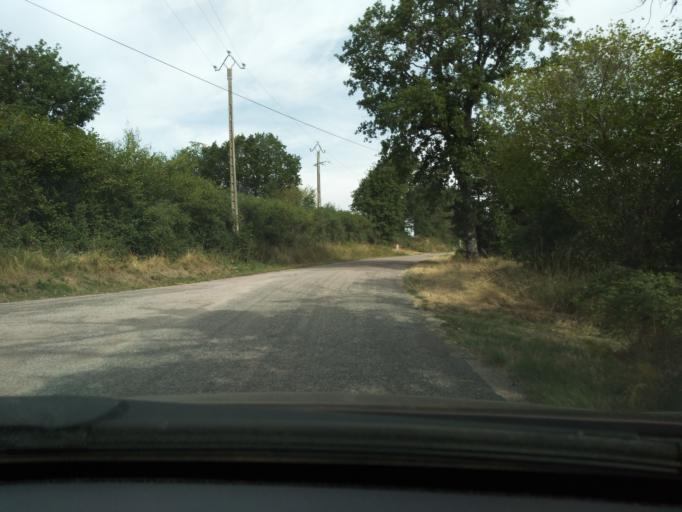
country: FR
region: Bourgogne
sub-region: Departement de la Cote-d'Or
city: Saulieu
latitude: 47.3825
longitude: 4.0762
